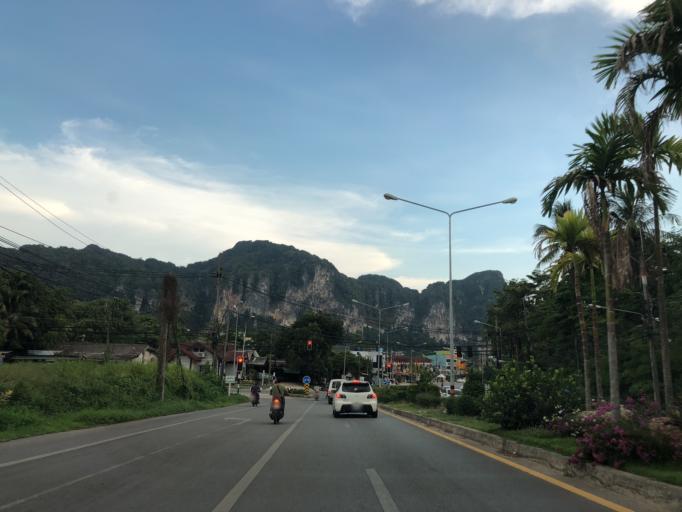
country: TH
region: Phangnga
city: Ban Ao Nang
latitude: 8.0422
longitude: 98.8368
